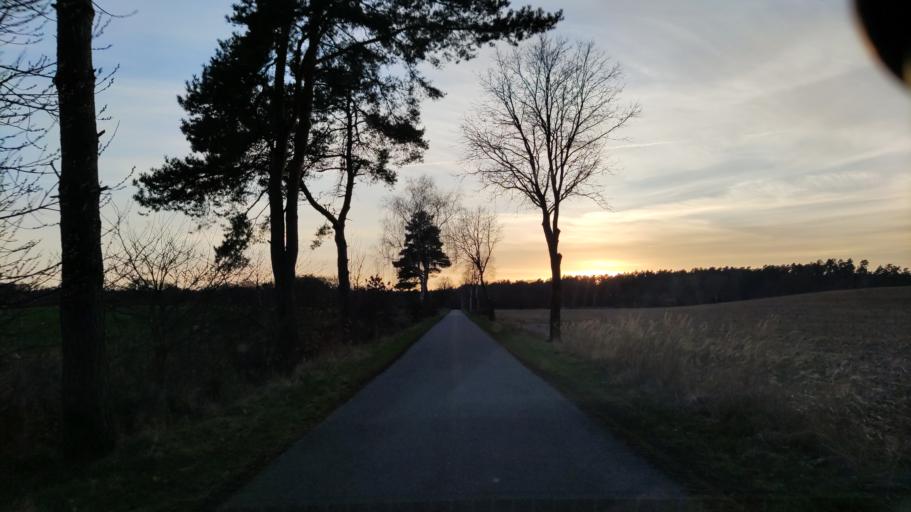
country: DE
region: Lower Saxony
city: Thomasburg
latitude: 53.2064
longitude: 10.6890
